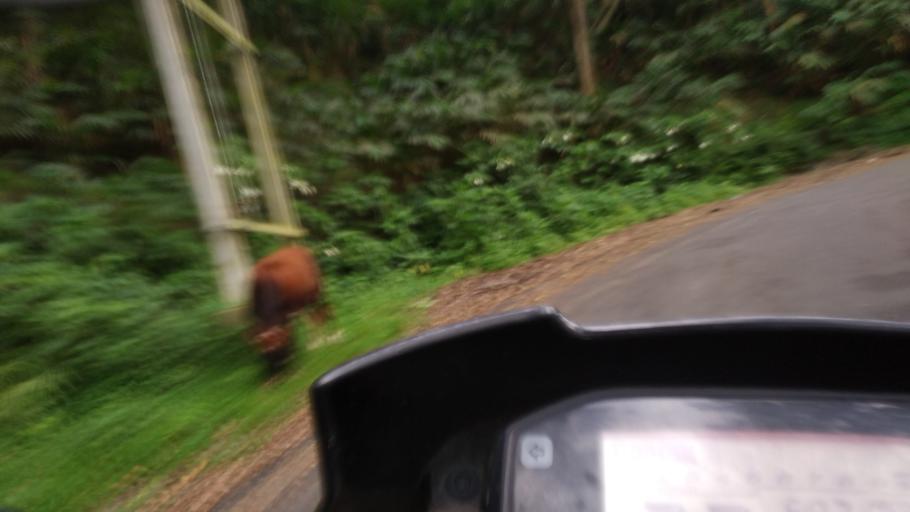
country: IN
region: Tamil Nadu
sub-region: Theni
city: Bodinayakkanur
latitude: 10.0338
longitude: 77.2304
